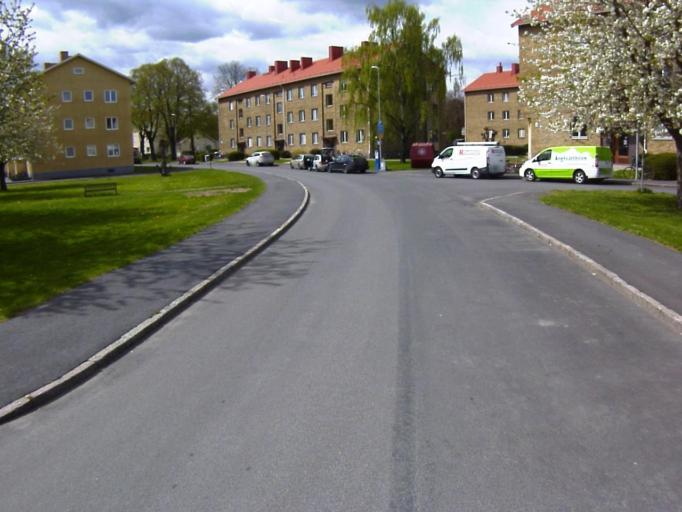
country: SE
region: Skane
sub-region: Kristianstads Kommun
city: Kristianstad
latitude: 56.0341
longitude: 14.1687
